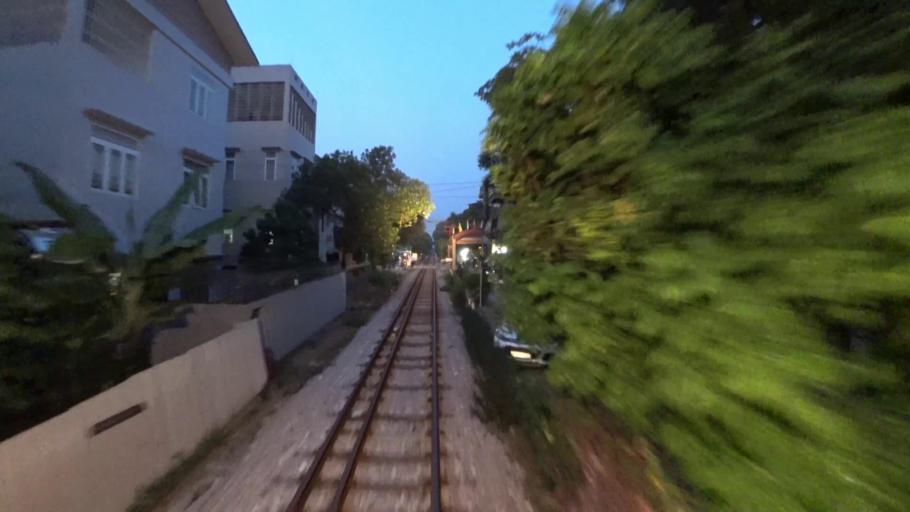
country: VN
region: Ha Noi
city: Soc Son
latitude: 21.2531
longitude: 105.8618
